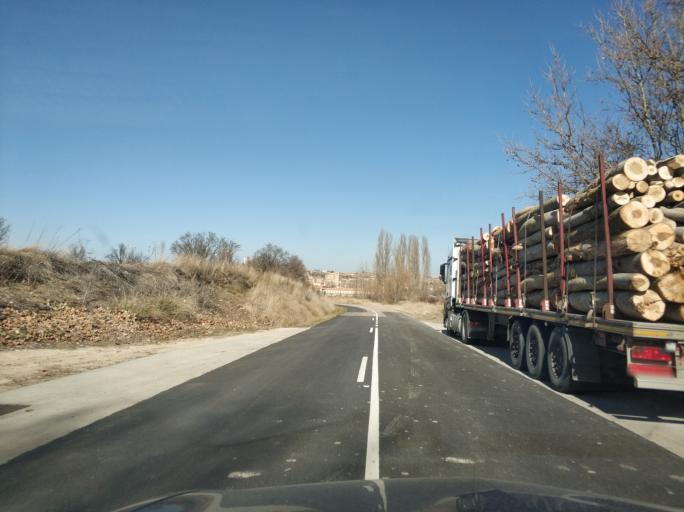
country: ES
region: Castille and Leon
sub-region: Provincia de Burgos
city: Penaranda de Duero
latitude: 41.6772
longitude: -3.4796
